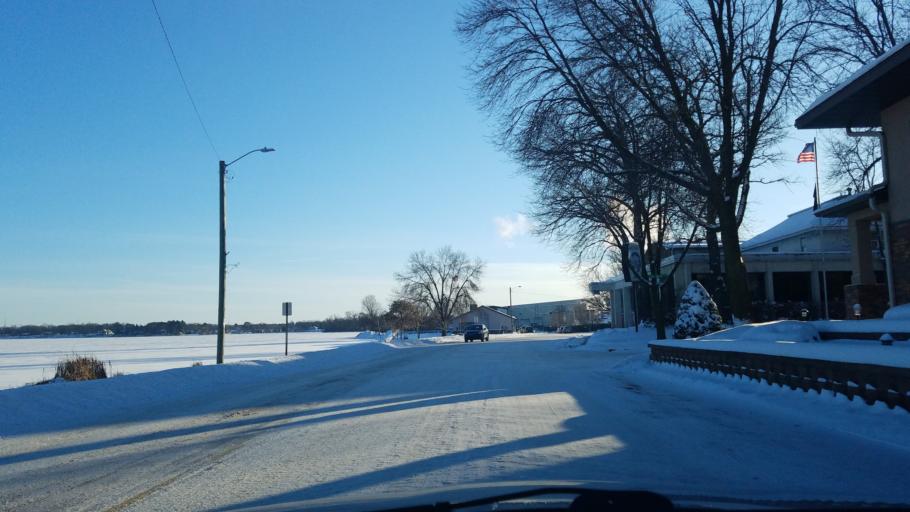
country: US
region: Wisconsin
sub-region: Barron County
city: Rice Lake
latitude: 45.5038
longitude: -91.7308
